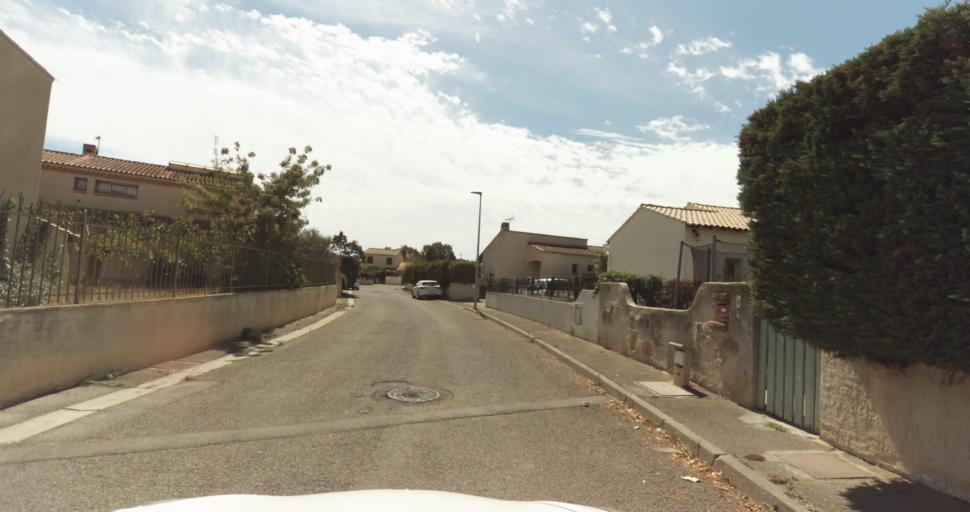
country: FR
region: Provence-Alpes-Cote d'Azur
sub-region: Departement des Bouches-du-Rhone
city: Miramas
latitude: 43.5832
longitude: 5.0114
